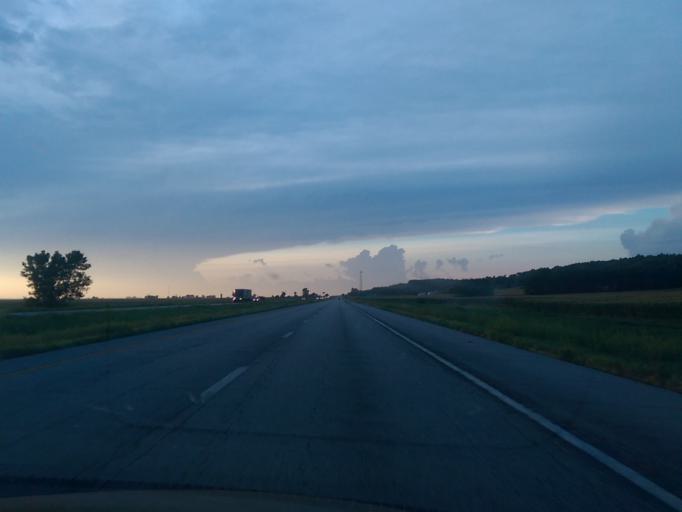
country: US
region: Missouri
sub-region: Atchison County
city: Rock Port
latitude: 40.3768
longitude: -95.5386
